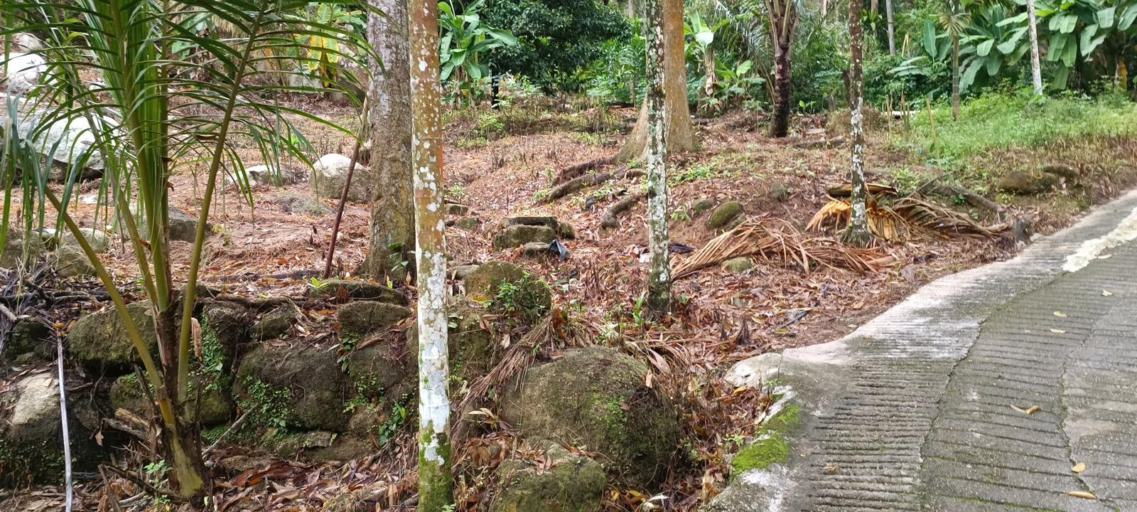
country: MY
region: Penang
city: Bukit Mertajam
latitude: 5.3732
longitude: 100.4787
